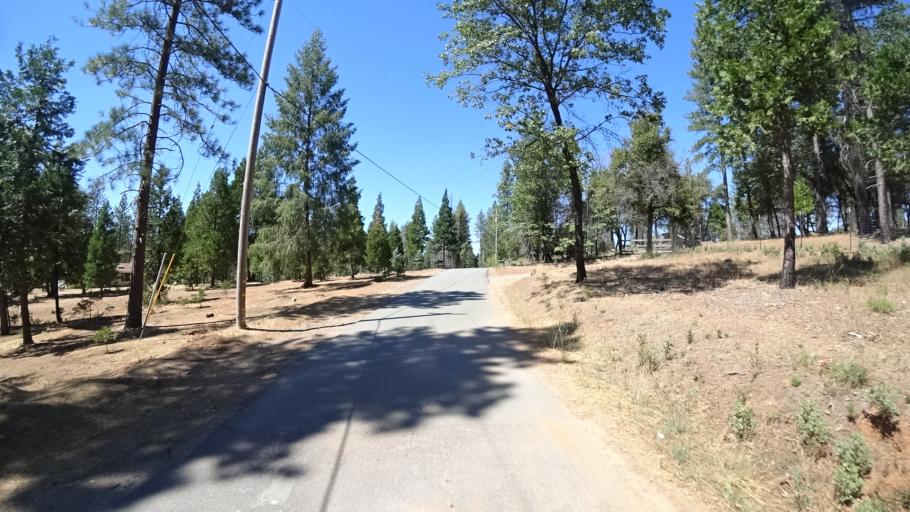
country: US
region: California
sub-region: Calaveras County
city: Mountain Ranch
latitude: 38.2831
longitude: -120.5396
